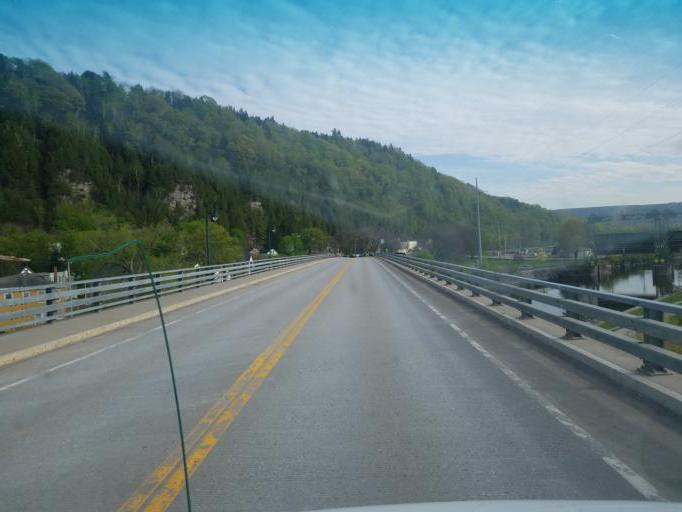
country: US
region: New York
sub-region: Herkimer County
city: Little Falls
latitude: 43.0392
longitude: -74.8608
